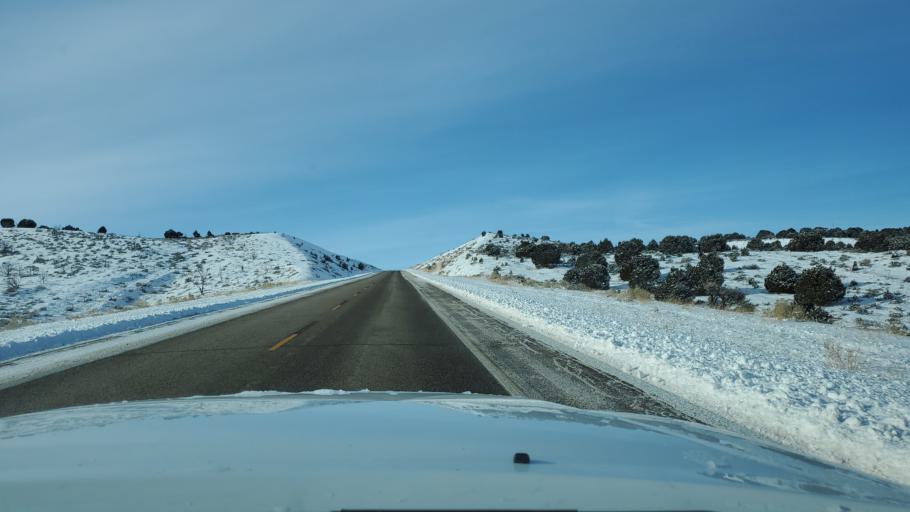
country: US
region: Colorado
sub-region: Rio Blanco County
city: Rangely
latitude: 40.3778
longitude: -108.3664
